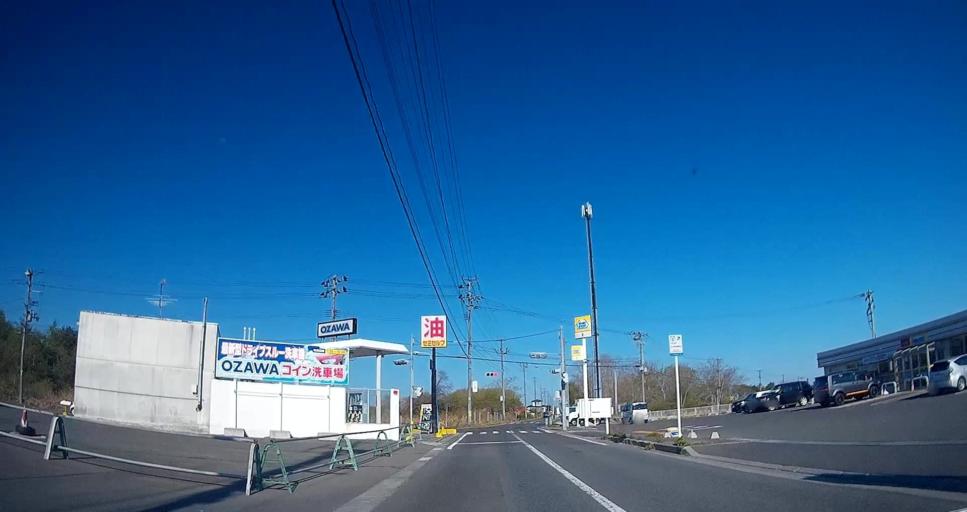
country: JP
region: Aomori
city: Hachinohe
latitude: 40.5202
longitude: 141.5724
